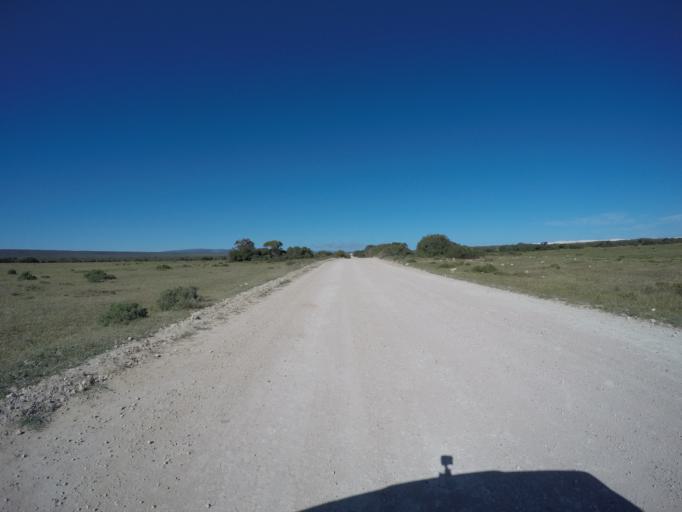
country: ZA
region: Western Cape
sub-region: Overberg District Municipality
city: Bredasdorp
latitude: -34.4547
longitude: 20.4211
